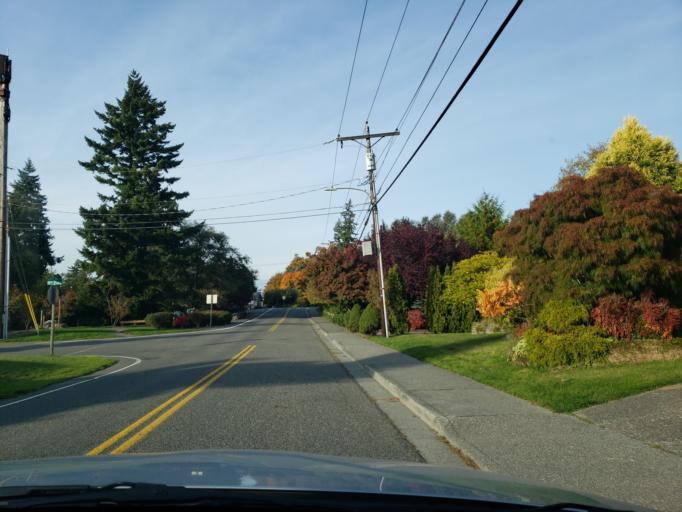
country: US
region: Washington
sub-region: Snohomish County
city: Mukilteo
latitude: 47.9373
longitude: -122.3012
